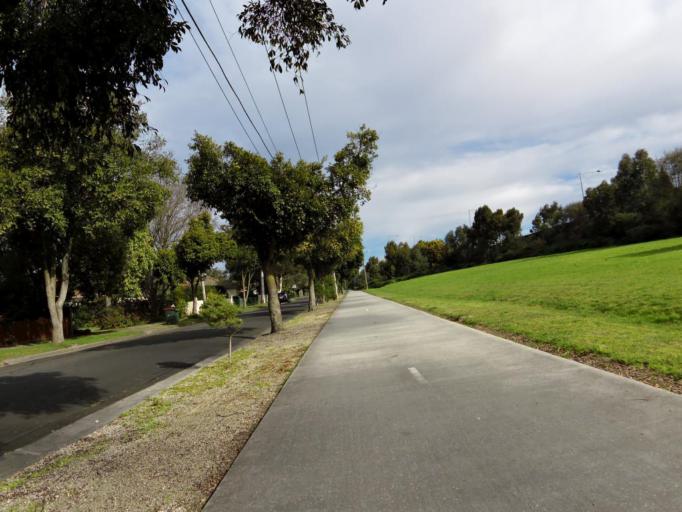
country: AU
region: Victoria
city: Mitcham
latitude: -37.8136
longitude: 145.2174
